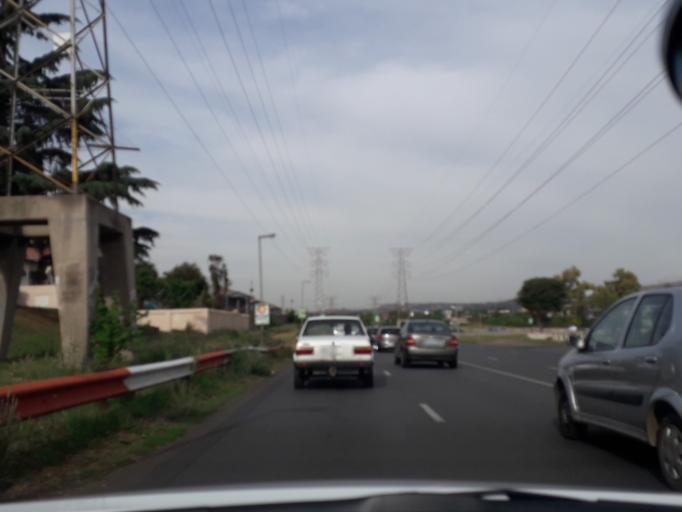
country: ZA
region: Gauteng
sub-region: City of Johannesburg Metropolitan Municipality
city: Johannesburg
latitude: -26.1779
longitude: 28.1072
